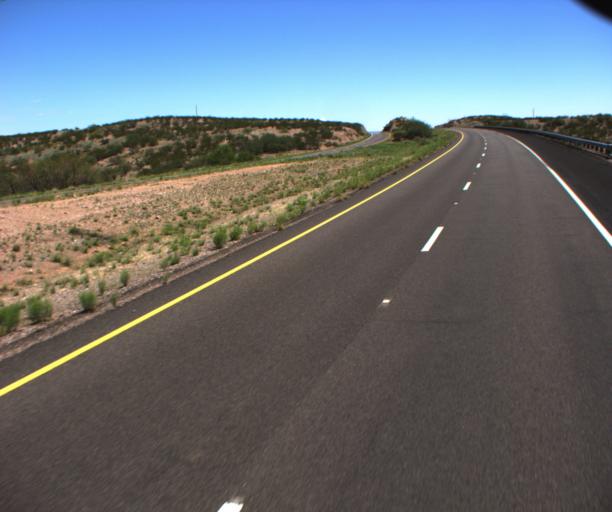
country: US
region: Arizona
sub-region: Greenlee County
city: Clifton
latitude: 32.9948
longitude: -109.2738
